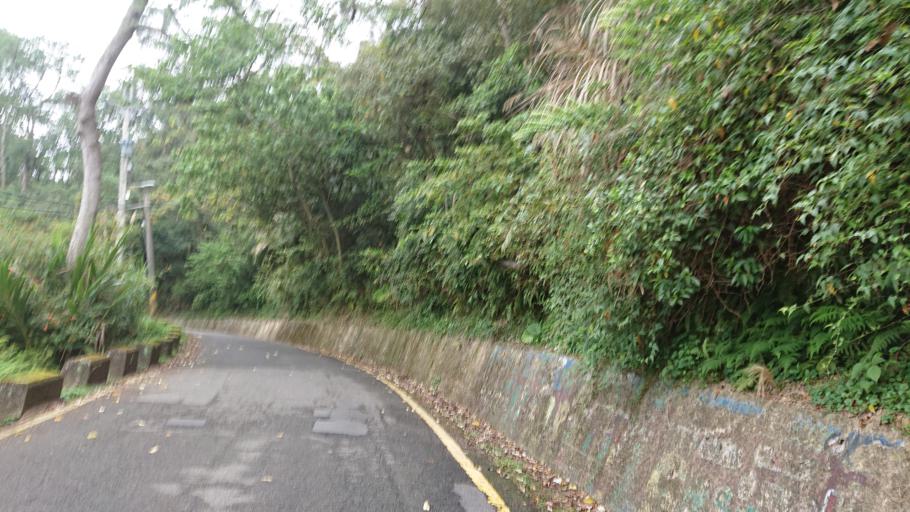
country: TW
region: Taiwan
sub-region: Taoyuan
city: Taoyuan
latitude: 24.9321
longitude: 121.3597
